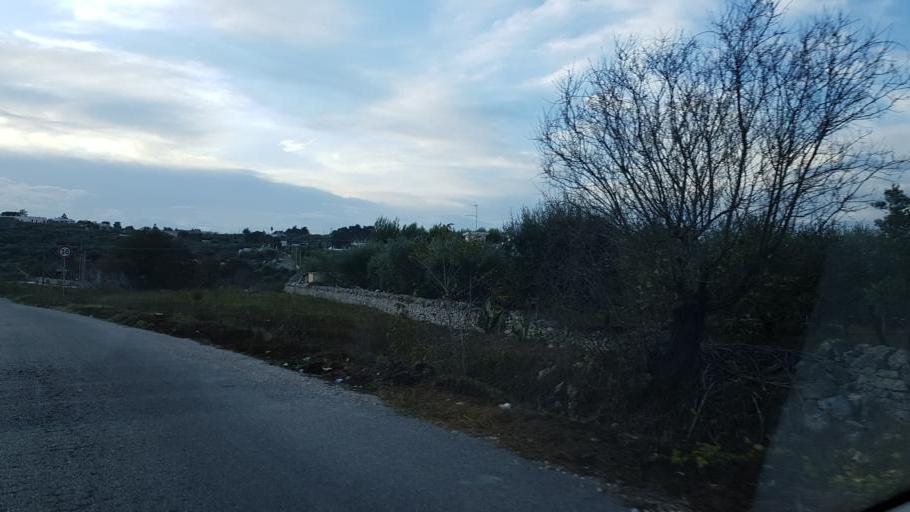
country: IT
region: Apulia
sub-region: Provincia di Bari
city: Locorotondo
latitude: 40.7645
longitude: 17.3272
